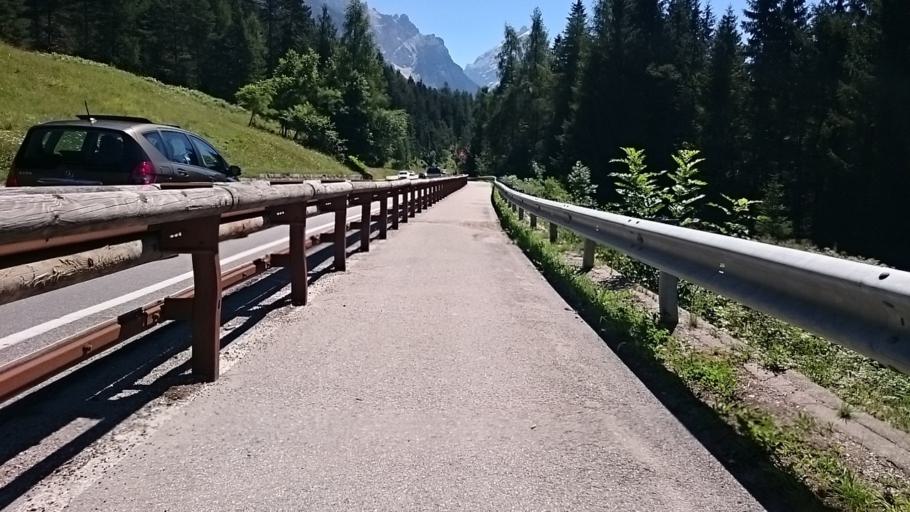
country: IT
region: Veneto
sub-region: Provincia di Belluno
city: Cortina d'Ampezzo
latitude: 46.5130
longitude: 12.1507
